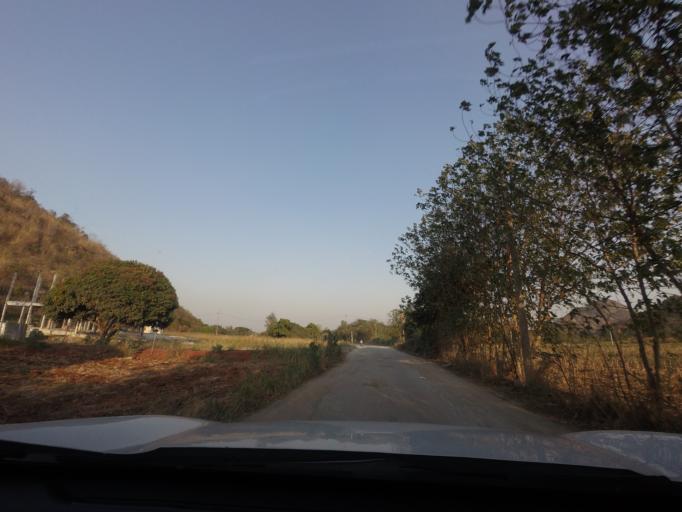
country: TH
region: Nakhon Ratchasima
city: Pak Chong
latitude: 14.6403
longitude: 101.3666
